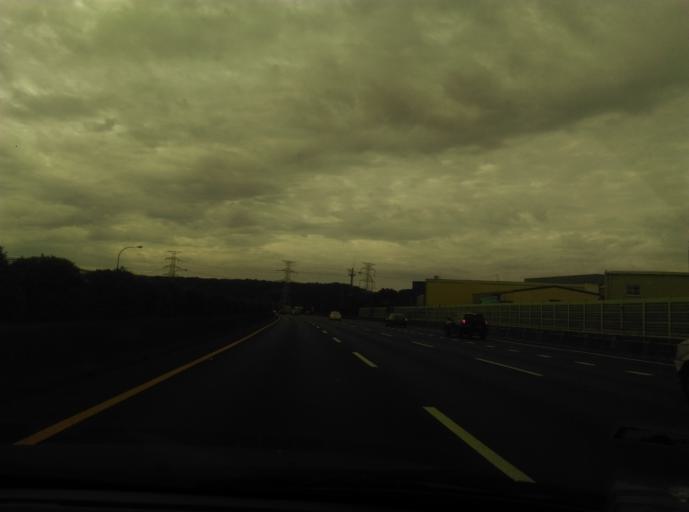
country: TW
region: Taiwan
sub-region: Taoyuan
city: Taoyuan
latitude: 24.9390
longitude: 121.3337
